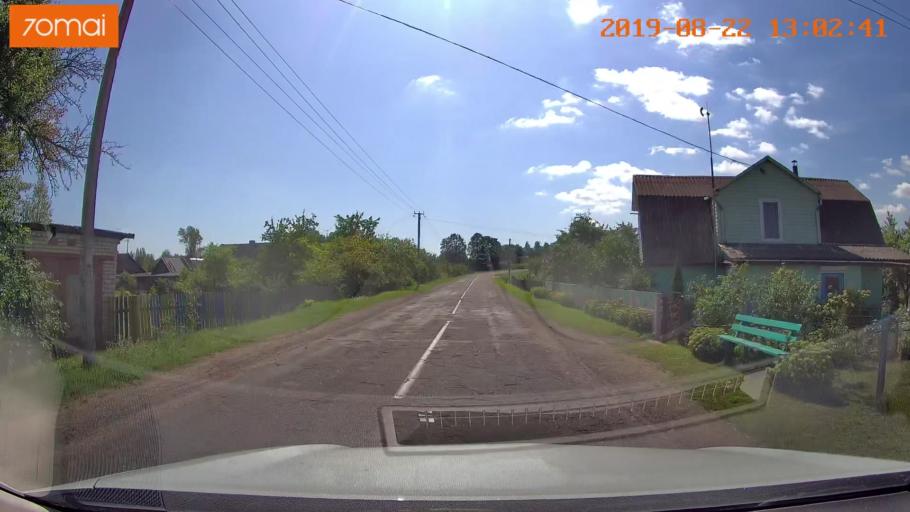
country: BY
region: Minsk
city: Prawdzinski
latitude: 53.3866
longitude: 27.8253
